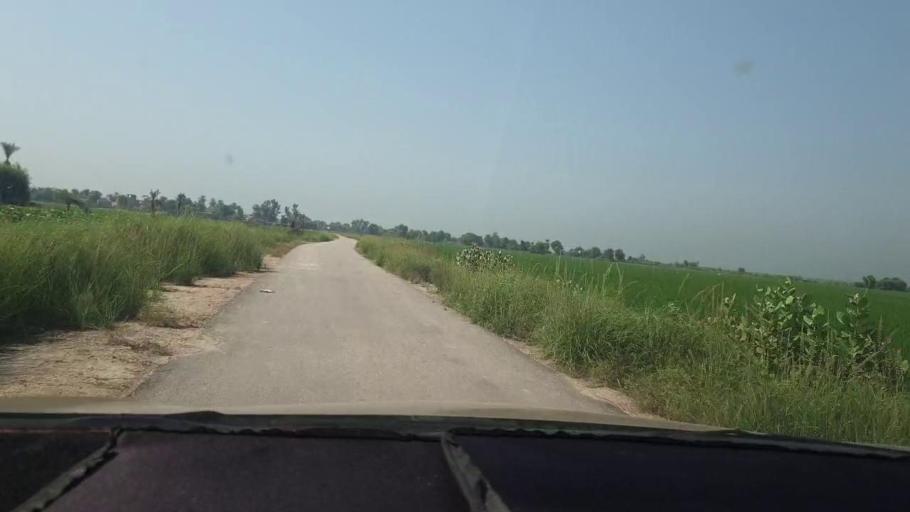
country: PK
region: Sindh
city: Kambar
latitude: 27.5597
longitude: 68.0429
